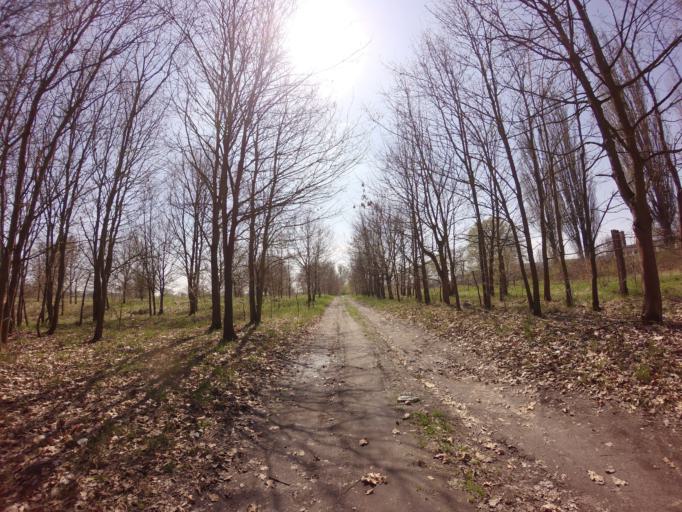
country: PL
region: West Pomeranian Voivodeship
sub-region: Powiat choszczenski
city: Choszczno
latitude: 53.1654
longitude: 15.4439
